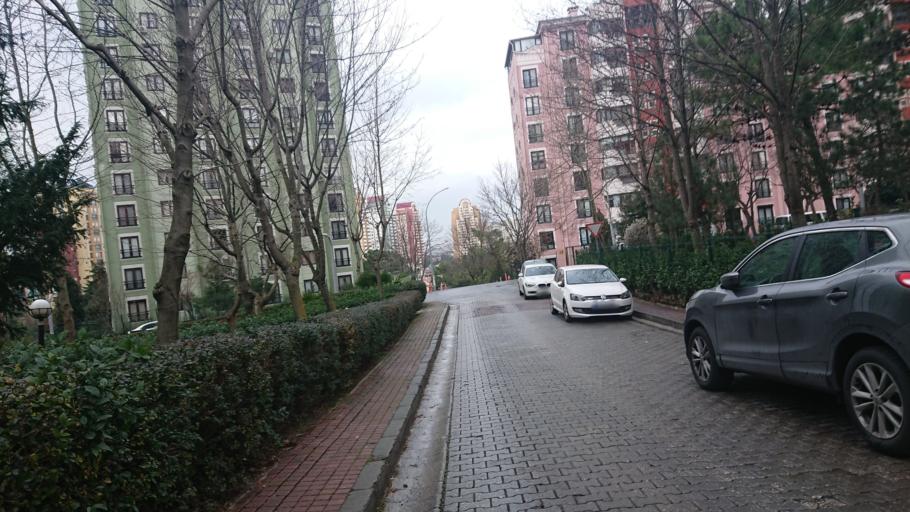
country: TR
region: Istanbul
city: Esenyurt
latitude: 41.0660
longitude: 28.6798
